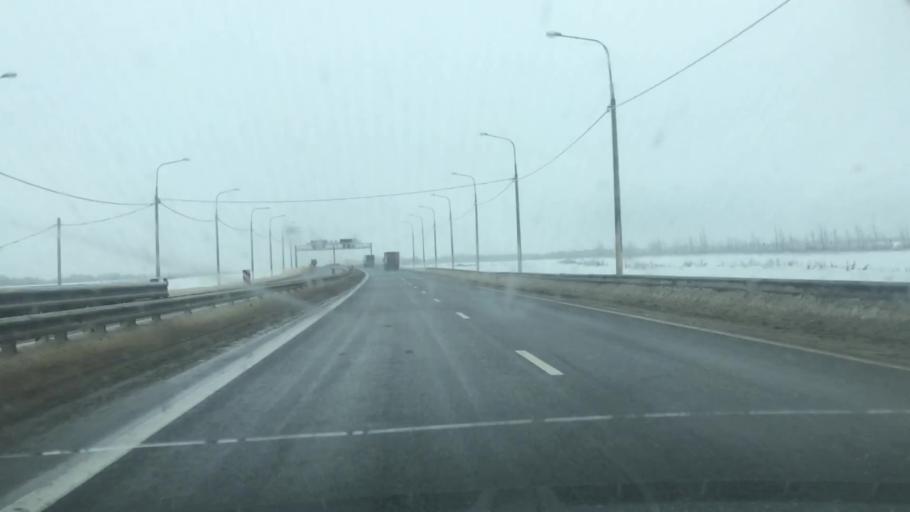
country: RU
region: Lipetsk
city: Stanovoye
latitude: 52.8976
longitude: 38.2258
